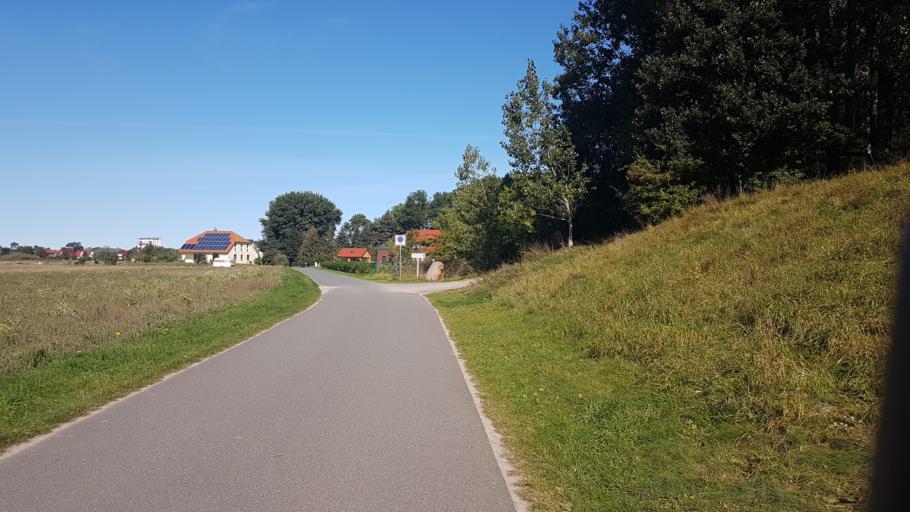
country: DE
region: Mecklenburg-Vorpommern
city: Glowe
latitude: 54.5642
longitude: 13.4766
